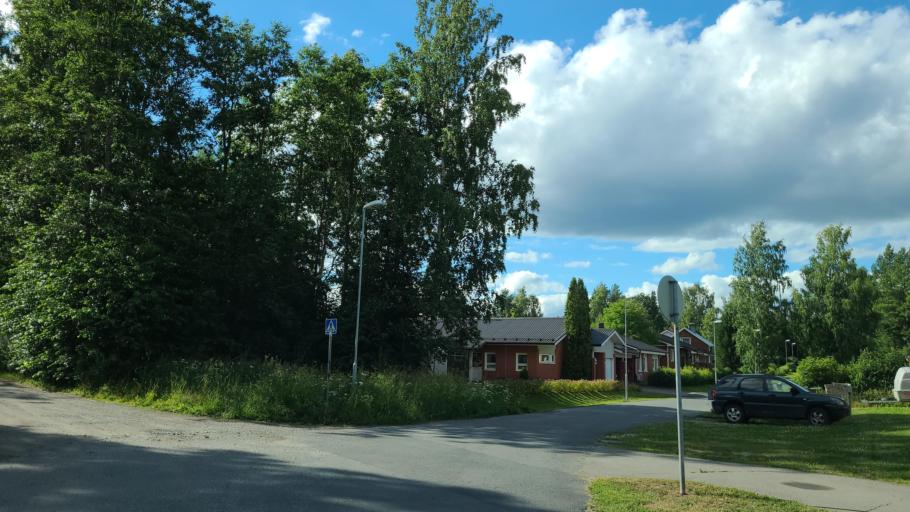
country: FI
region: Northern Savo
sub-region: Kuopio
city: Kuopio
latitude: 62.9260
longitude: 27.6275
